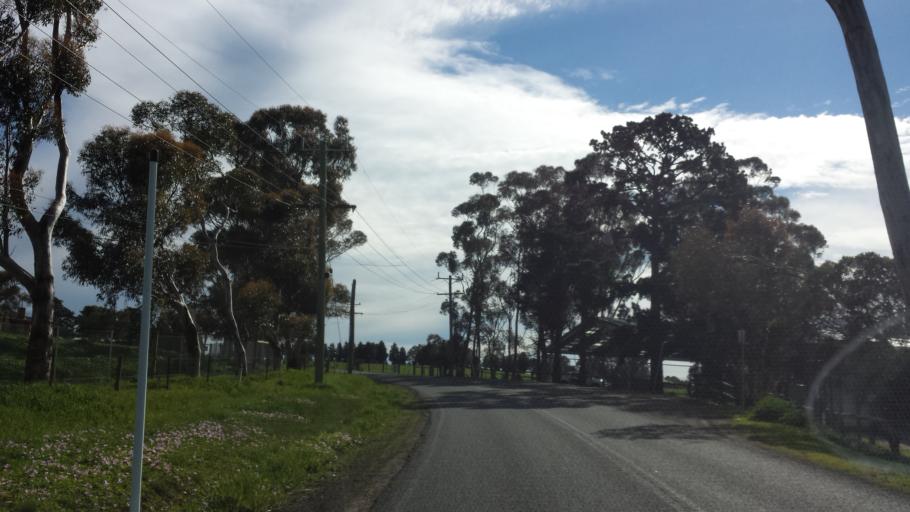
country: AU
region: Victoria
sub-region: Nillumbik
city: Doreen
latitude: -37.6067
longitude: 145.1464
